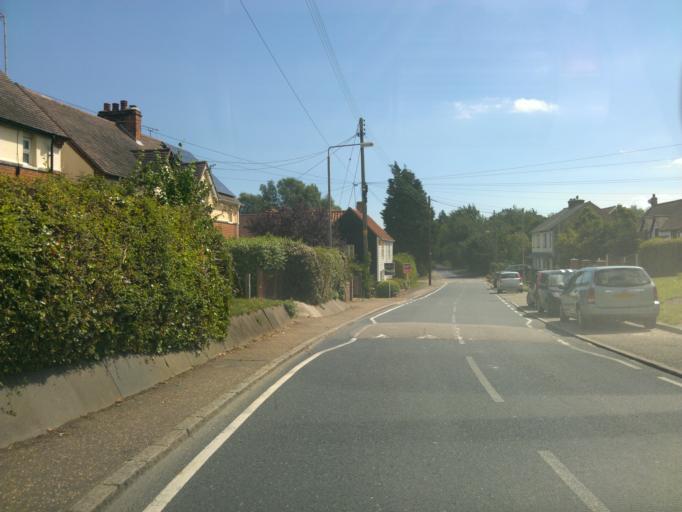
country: GB
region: England
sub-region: Essex
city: Saint Osyth
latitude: 51.7972
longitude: 1.0804
